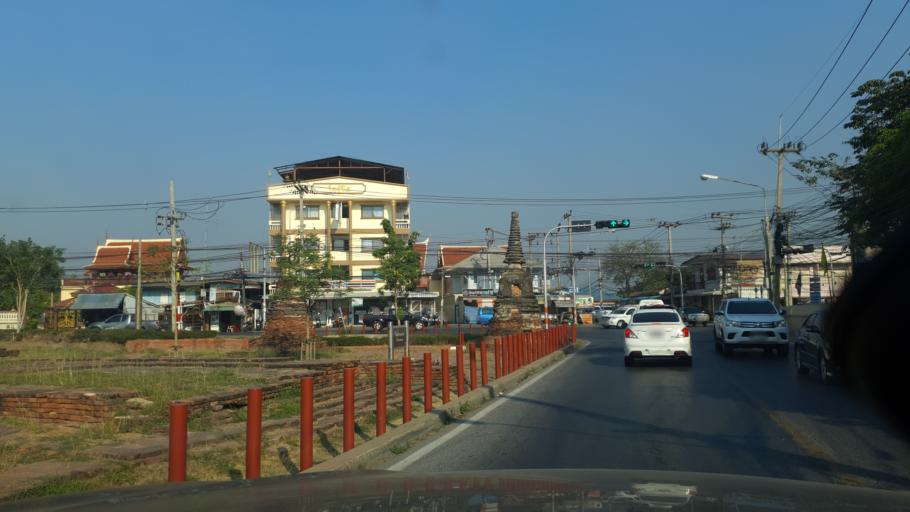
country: TH
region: Phra Nakhon Si Ayutthaya
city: Phra Nakhon Si Ayutthaya
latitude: 14.3621
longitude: 100.5681
